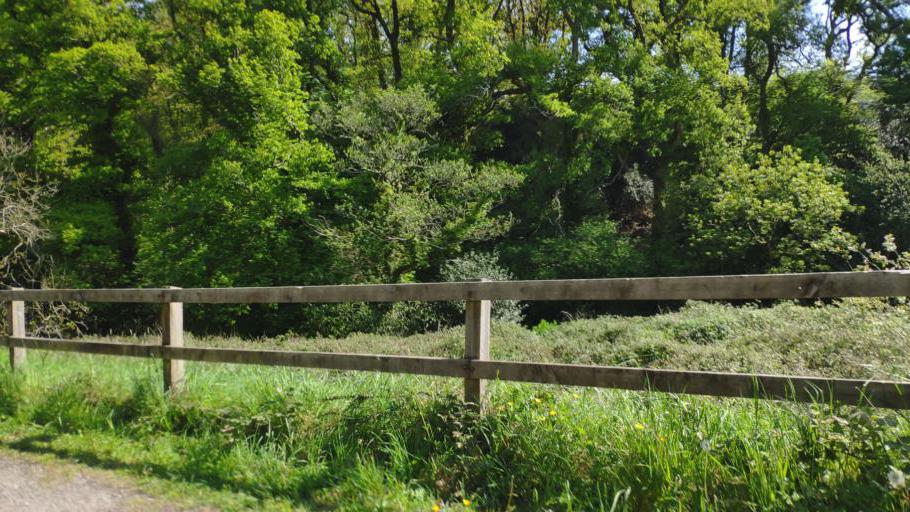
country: IE
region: Munster
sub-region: County Cork
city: Blarney
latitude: 51.9400
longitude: -8.5639
